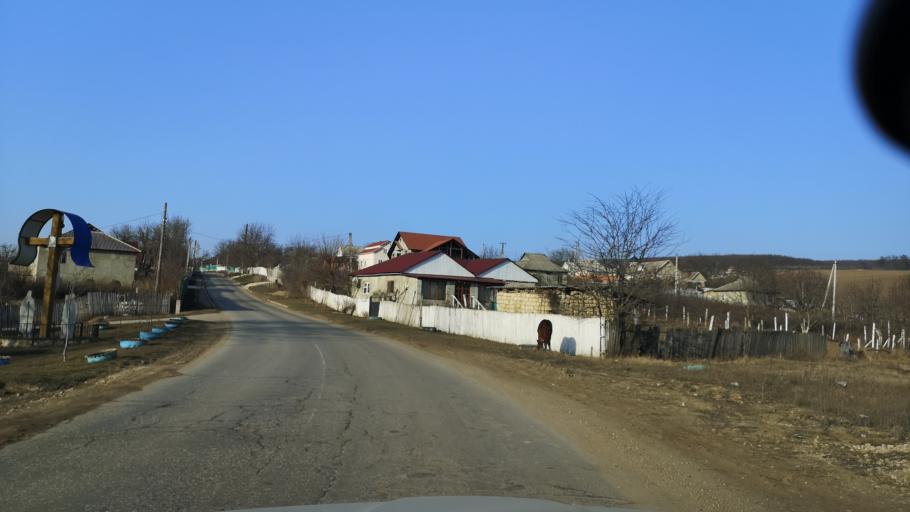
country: MD
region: Stinga Nistrului
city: Bucovat
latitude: 47.1107
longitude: 28.5103
